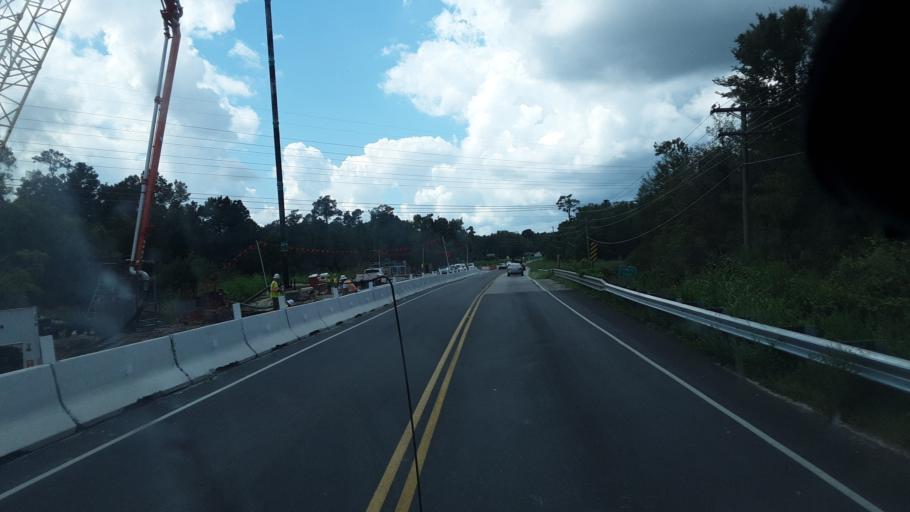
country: US
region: South Carolina
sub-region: Williamsburg County
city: Andrews
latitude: 33.3708
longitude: -79.4495
